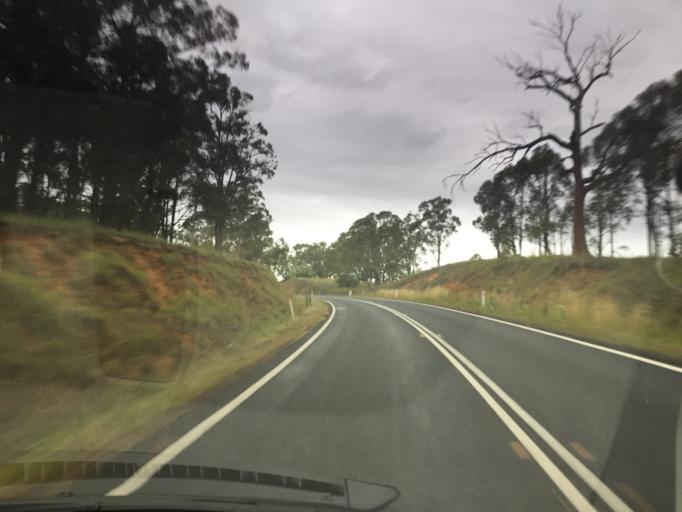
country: AU
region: New South Wales
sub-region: Bega Valley
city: Bega
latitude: -36.6369
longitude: 149.5774
